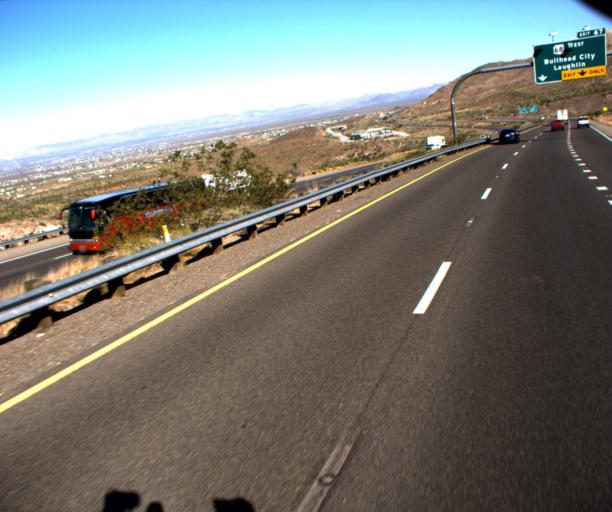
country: US
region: Arizona
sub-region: Mohave County
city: Kingman
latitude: 35.2139
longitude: -114.1138
